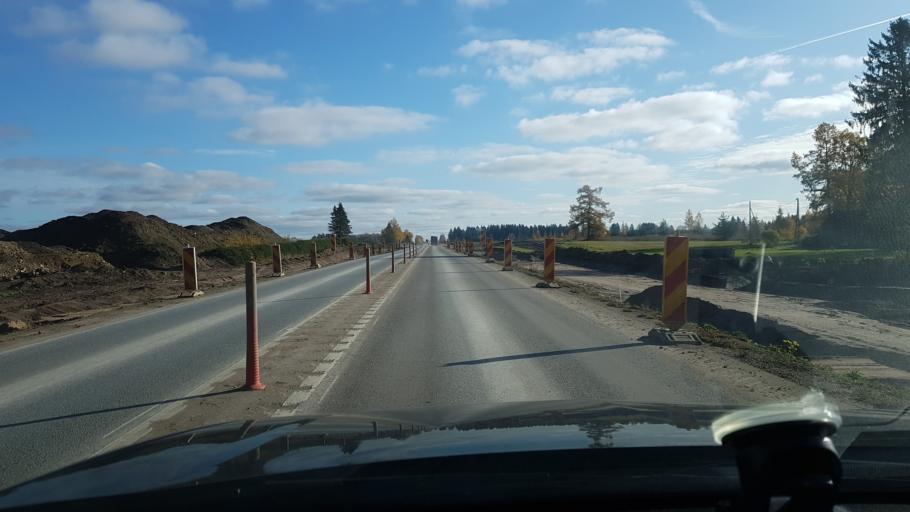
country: EE
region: Laeaene-Virumaa
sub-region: Kadrina vald
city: Kadrina
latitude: 59.4371
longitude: 26.1509
